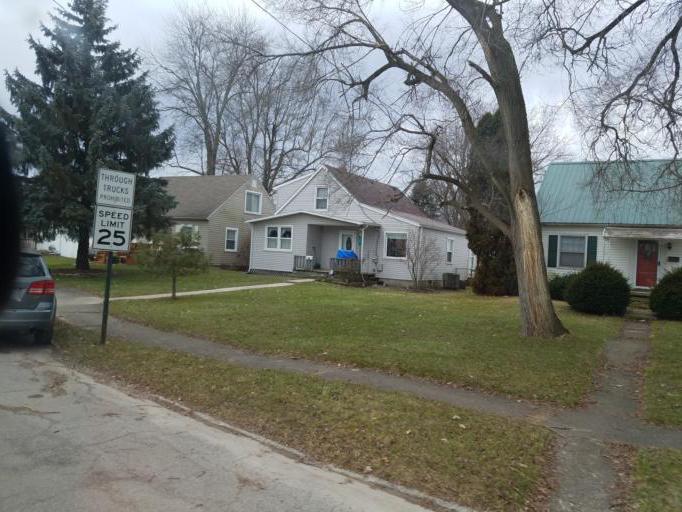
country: US
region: Ohio
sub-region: Marion County
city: Marion
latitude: 40.5937
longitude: -83.1044
